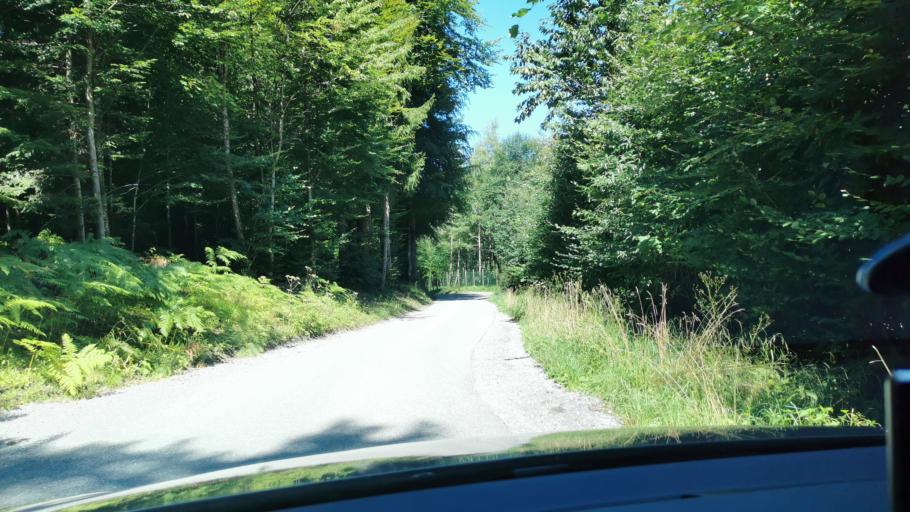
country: AT
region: Vorarlberg
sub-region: Politischer Bezirk Feldkirch
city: Viktorsberg
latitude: 47.2865
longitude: 9.6719
